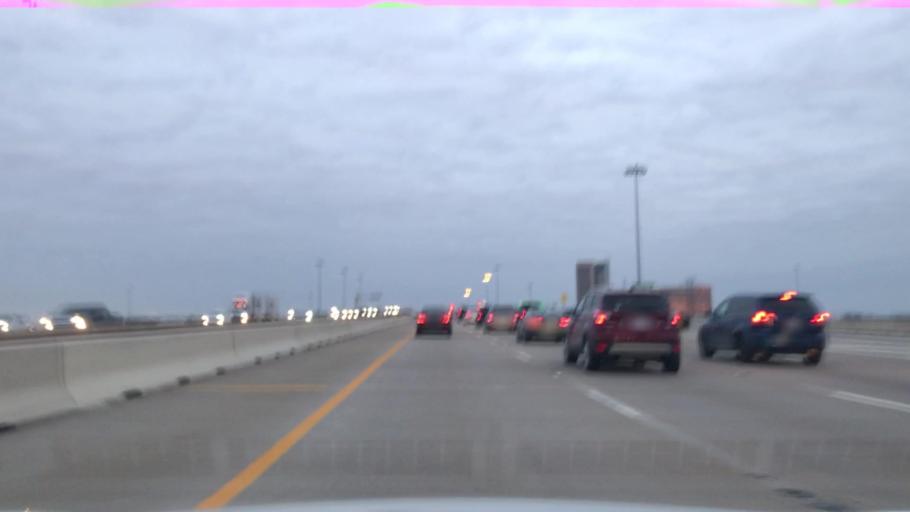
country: US
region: Texas
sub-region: Collin County
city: Plano
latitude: 33.0038
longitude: -96.7152
